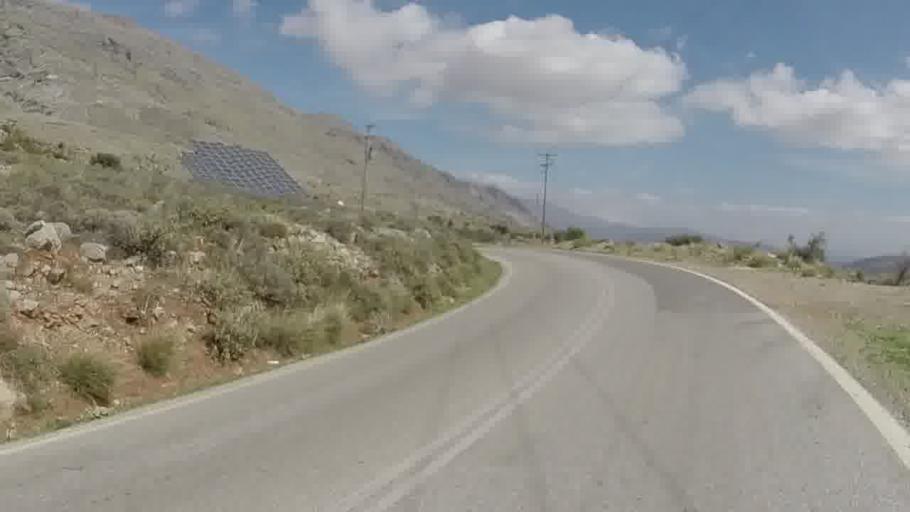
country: GR
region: Crete
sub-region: Nomos Rethymnis
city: Agia Galini
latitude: 35.1507
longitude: 24.6219
